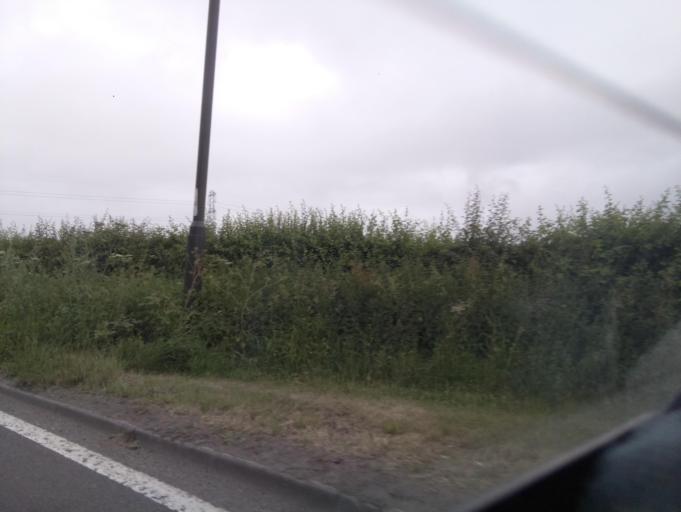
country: GB
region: England
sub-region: Staffordshire
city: Burton upon Trent
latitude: 52.7774
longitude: -1.6059
